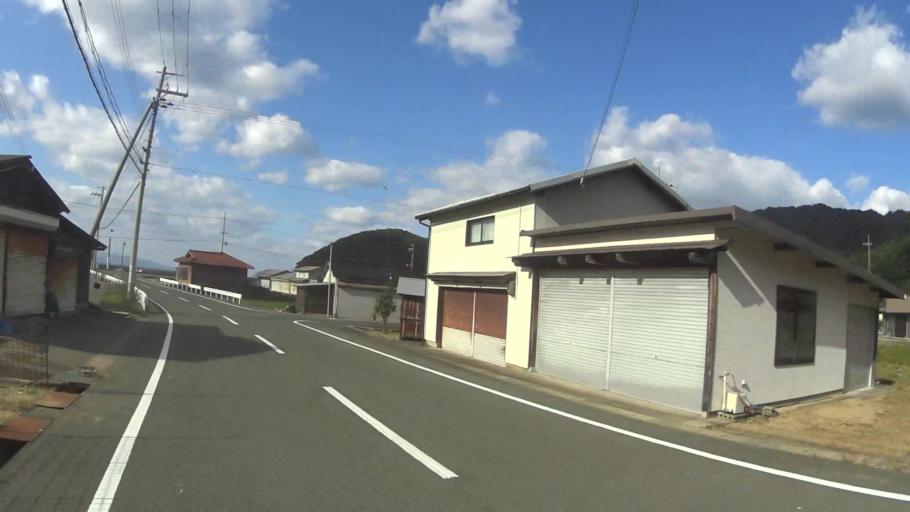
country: JP
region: Kyoto
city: Maizuru
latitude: 35.5645
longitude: 135.4257
